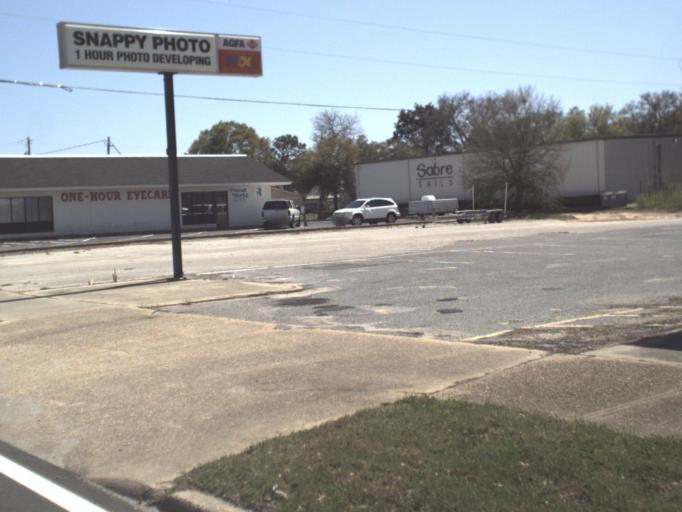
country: US
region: Florida
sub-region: Okaloosa County
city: Fort Walton Beach
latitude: 30.4152
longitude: -86.6065
